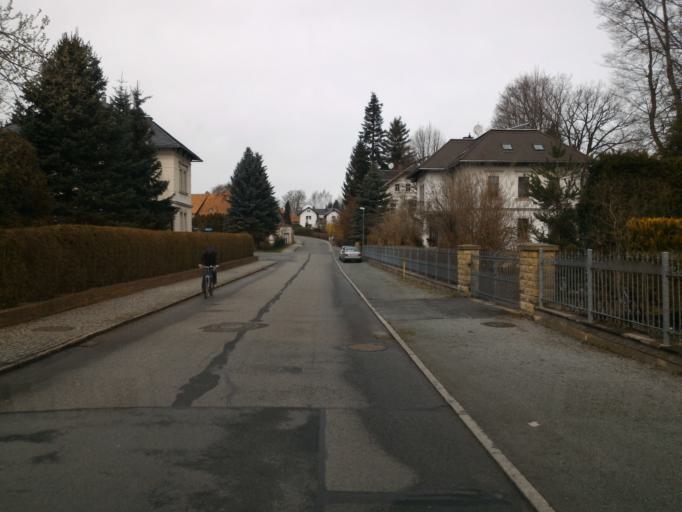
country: DE
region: Saxony
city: Ebersbach
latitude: 51.0077
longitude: 14.5789
